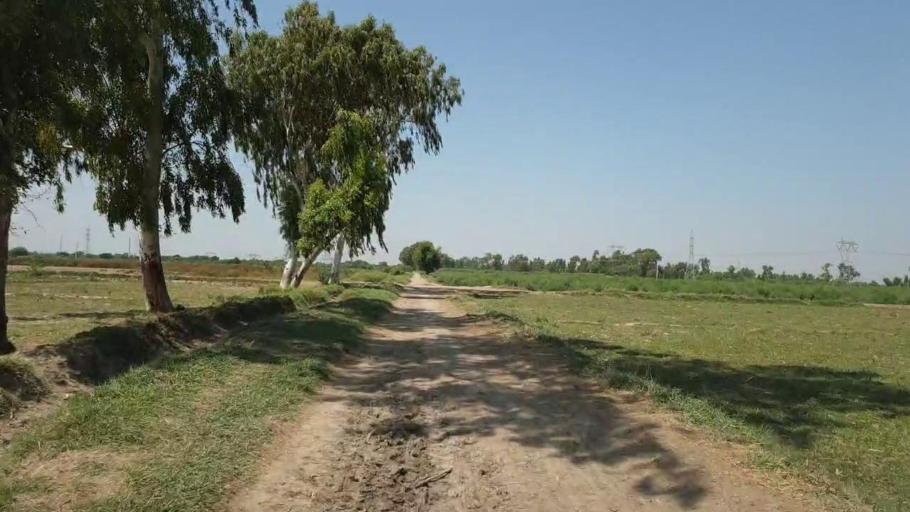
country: PK
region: Sindh
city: Hyderabad
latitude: 25.4749
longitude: 68.4181
